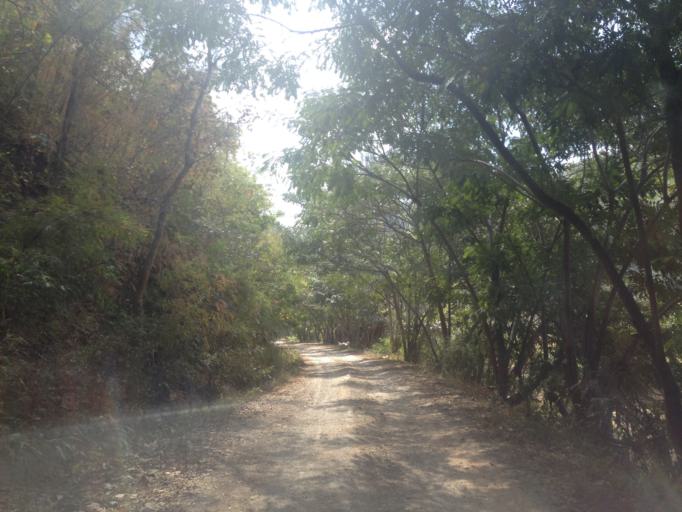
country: TH
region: Mae Hong Son
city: Ban Huai I Huak
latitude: 18.0962
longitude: 98.1896
